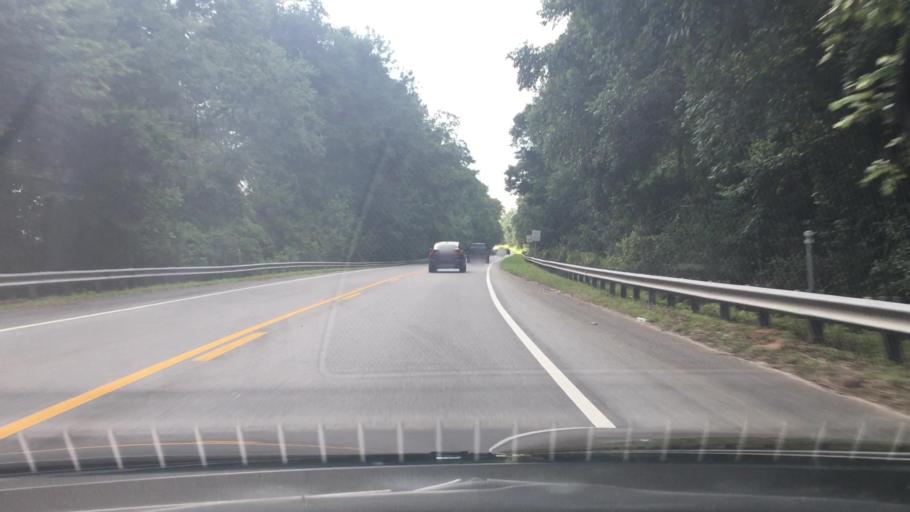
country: US
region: Georgia
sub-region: Coweta County
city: Senoia
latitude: 33.2568
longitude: -84.4980
